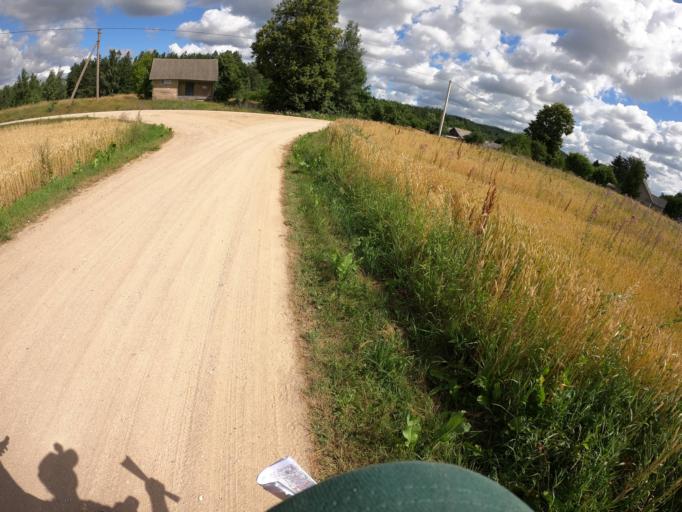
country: LT
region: Alytaus apskritis
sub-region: Alytus
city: Alytus
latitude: 54.3298
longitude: 24.0645
